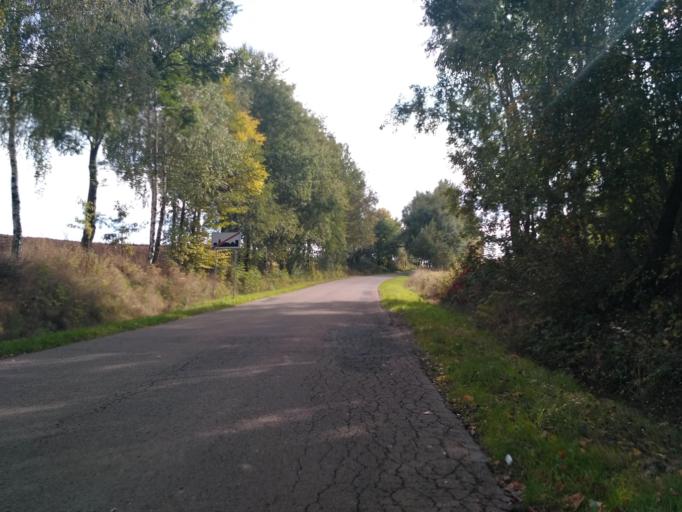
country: PL
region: Subcarpathian Voivodeship
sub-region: Powiat ropczycko-sedziszowski
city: Wielopole Skrzynskie
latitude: 49.9291
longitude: 21.5645
